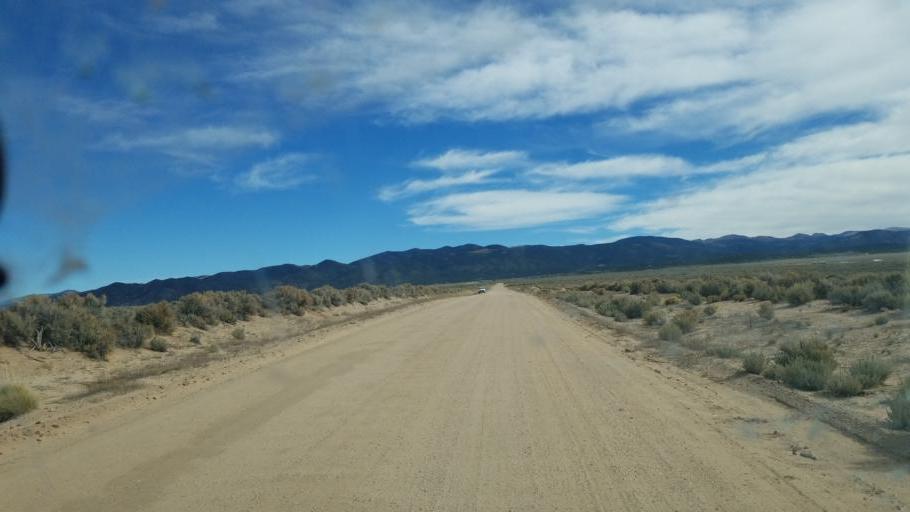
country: US
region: Colorado
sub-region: Costilla County
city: San Luis
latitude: 37.2868
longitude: -105.4391
